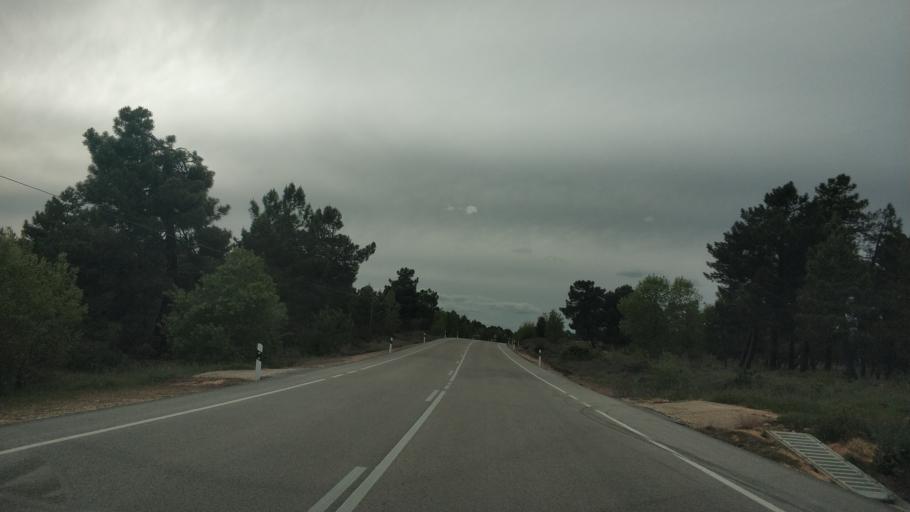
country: ES
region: Castille and Leon
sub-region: Provincia de Soria
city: Quintanas de Gormaz
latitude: 41.5299
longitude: -2.9459
